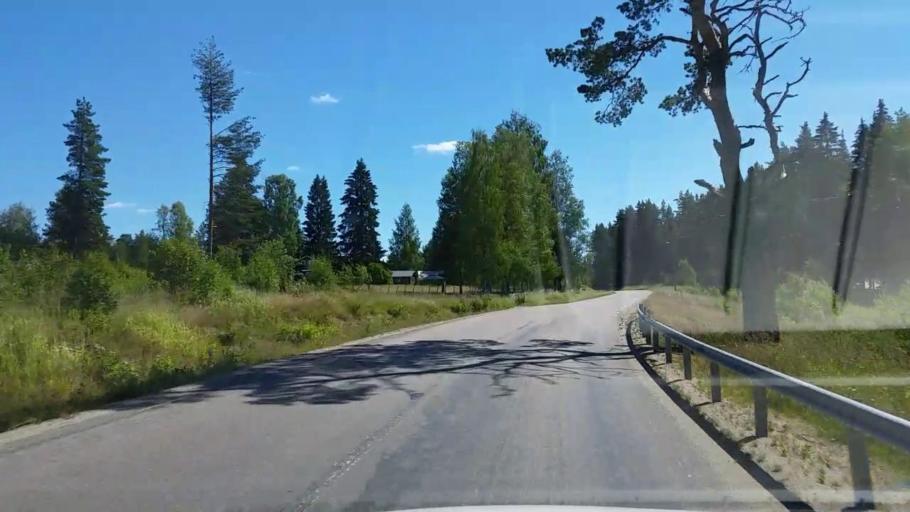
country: SE
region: Gaevleborg
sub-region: Ovanakers Kommun
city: Edsbyn
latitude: 61.4537
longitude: 15.7069
